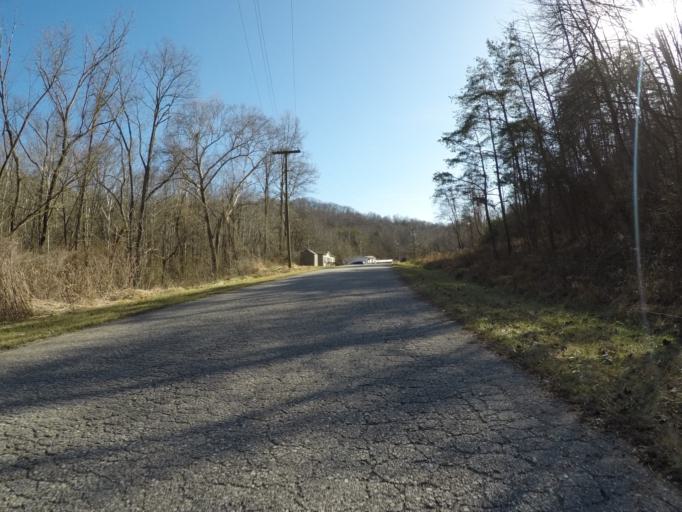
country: US
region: Kentucky
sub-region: Boyd County
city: Catlettsburg
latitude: 38.4191
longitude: -82.6091
